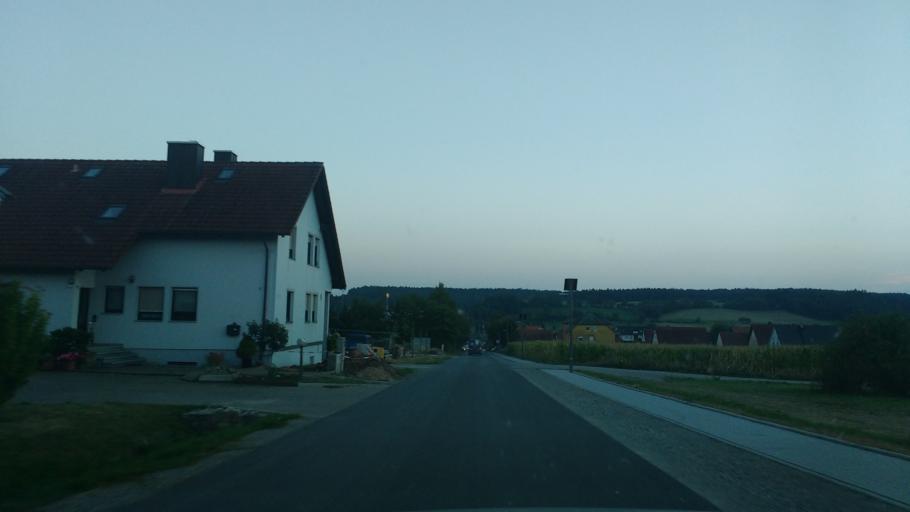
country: DE
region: Bavaria
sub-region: Regierungsbezirk Unterfranken
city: Geiselwind
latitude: 49.7777
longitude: 10.4701
